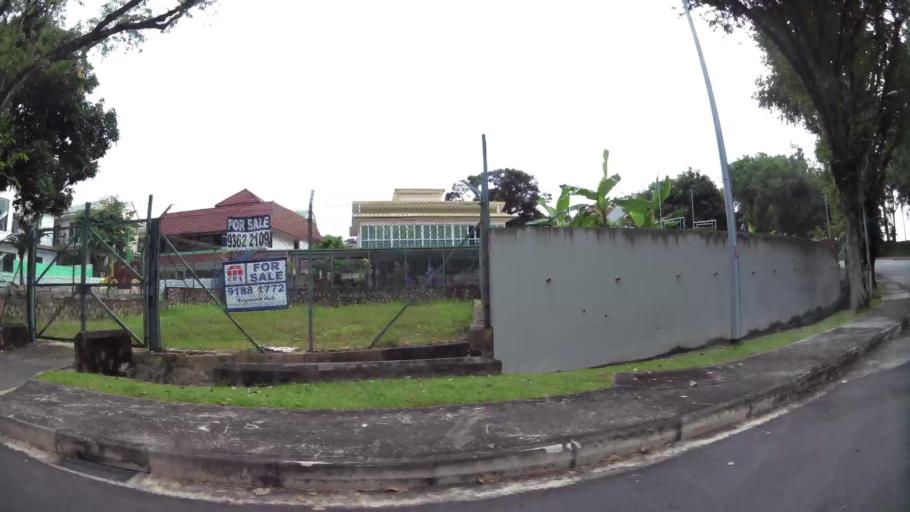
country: MY
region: Johor
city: Kampung Pasir Gudang Baru
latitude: 1.4197
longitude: 103.9089
